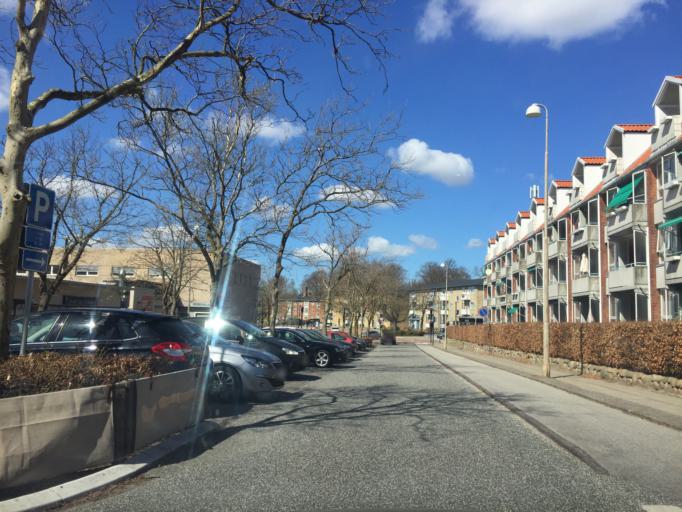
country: DK
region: Capital Region
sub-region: Rudersdal Kommune
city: Holte
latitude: 55.7948
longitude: 12.4752
